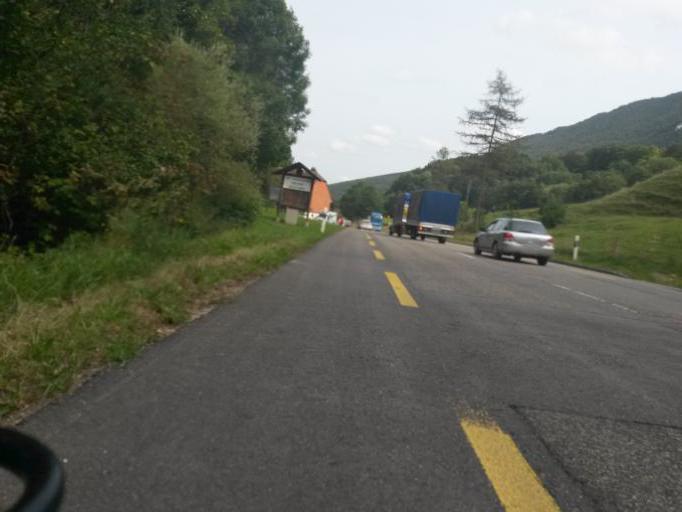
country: CH
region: Solothurn
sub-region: Bezirk Thal
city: Welschenrohr
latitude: 47.2806
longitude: 7.5422
